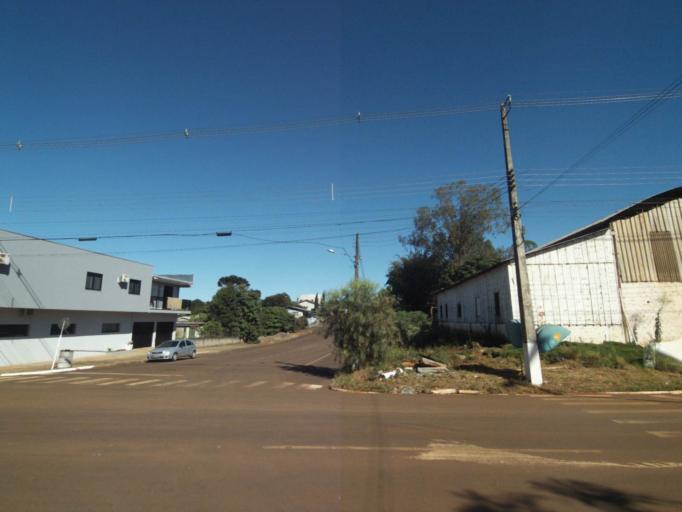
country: BR
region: Parana
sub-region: Pato Branco
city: Pato Branco
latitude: -26.2599
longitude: -52.7748
